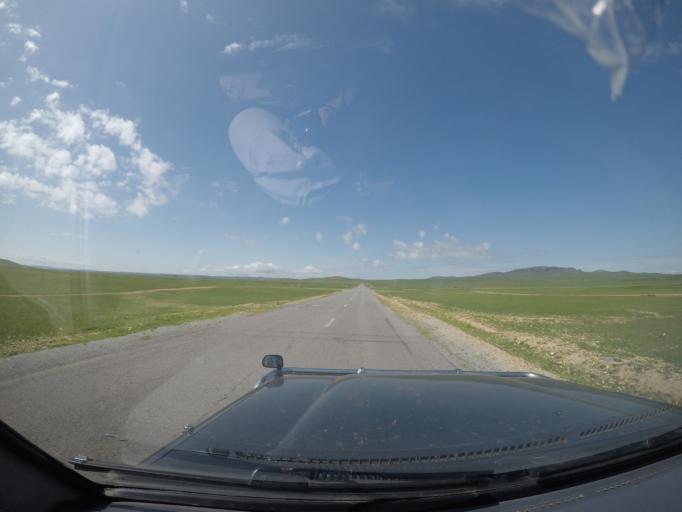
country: MN
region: Hentiy
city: Dundburd
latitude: 47.3399
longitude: 111.4683
